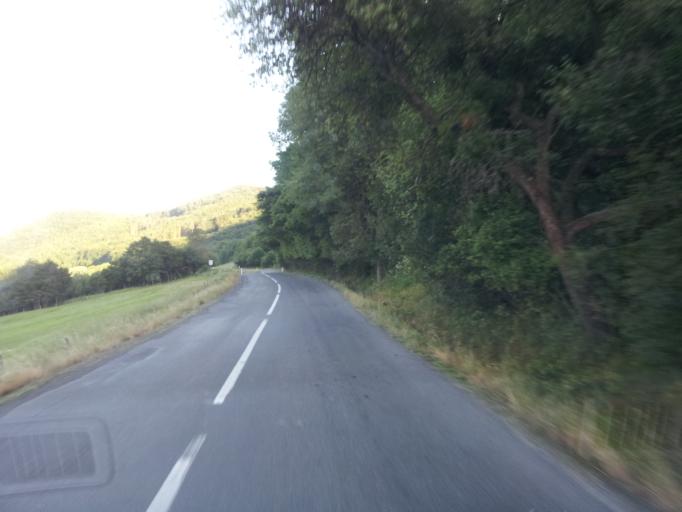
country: SK
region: Banskobystricky
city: Svaety Anton
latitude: 48.3378
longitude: 18.9512
